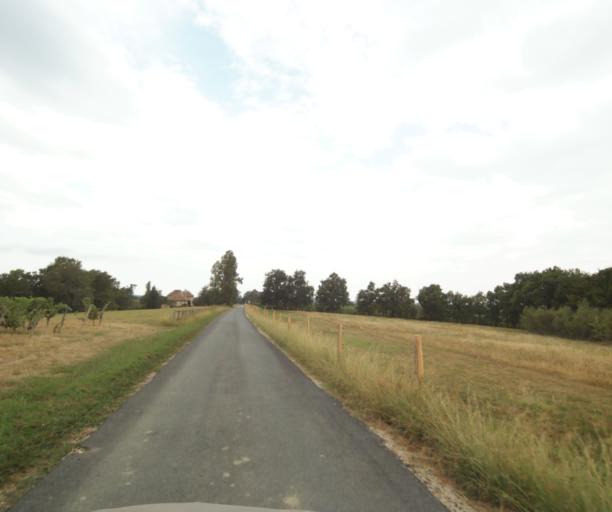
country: FR
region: Aquitaine
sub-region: Departement de la Gironde
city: Creon
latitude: 44.7529
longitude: -0.3455
